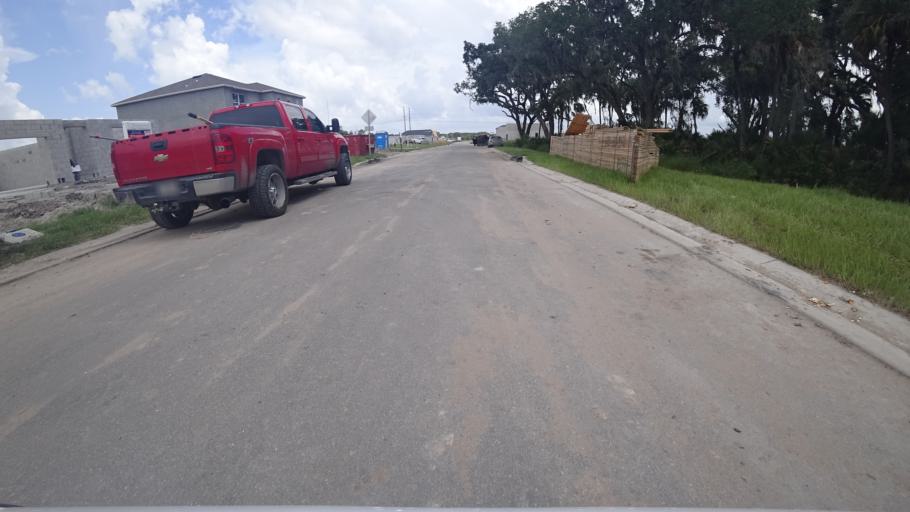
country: US
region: Florida
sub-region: Manatee County
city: Ellenton
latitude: 27.5494
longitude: -82.5132
